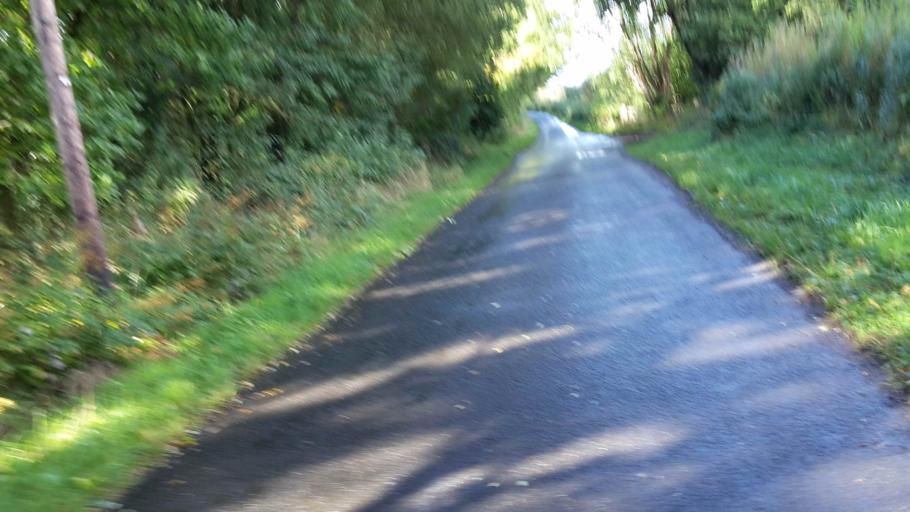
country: GB
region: Scotland
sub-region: South Lanarkshire
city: Law
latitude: 55.7253
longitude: -3.8645
